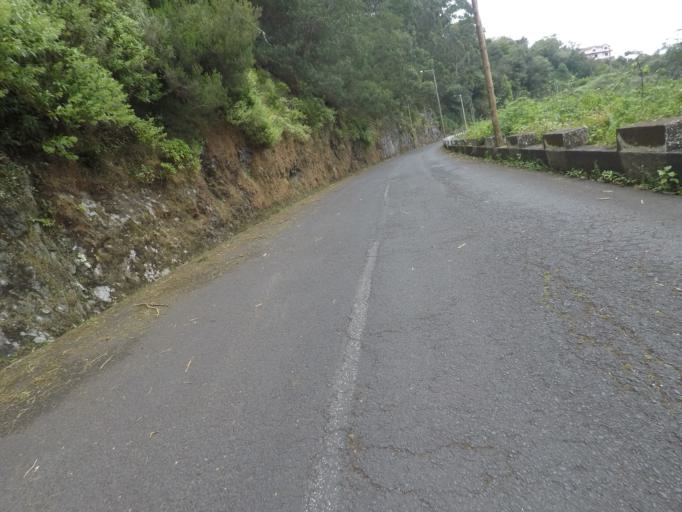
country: PT
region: Madeira
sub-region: Santana
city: Santana
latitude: 32.7947
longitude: -16.8637
